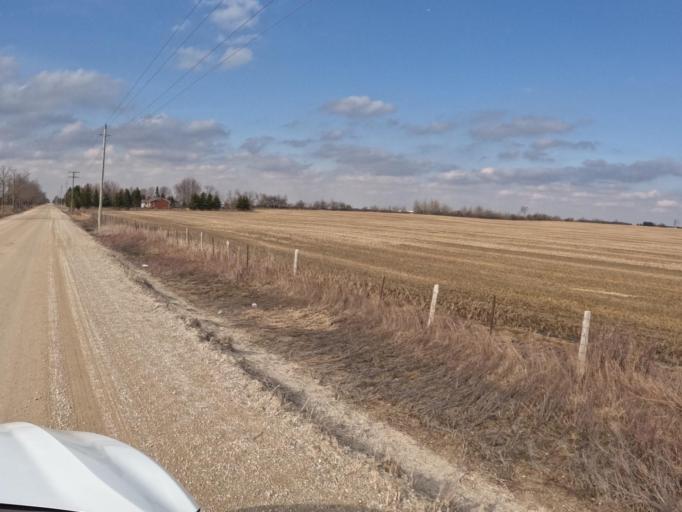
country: CA
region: Ontario
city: Shelburne
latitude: 43.9082
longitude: -80.3031
